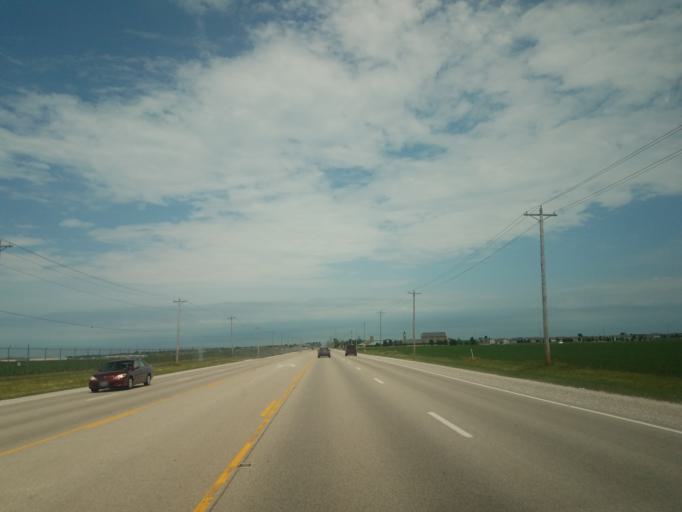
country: US
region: Illinois
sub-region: McLean County
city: Downs
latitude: 40.4821
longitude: -88.9024
